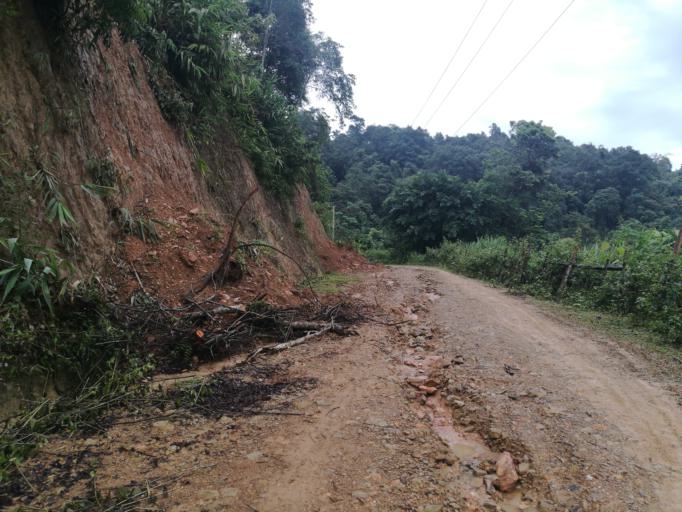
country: LA
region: Phongsali
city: Khoa
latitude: 21.2568
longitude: 102.6651
